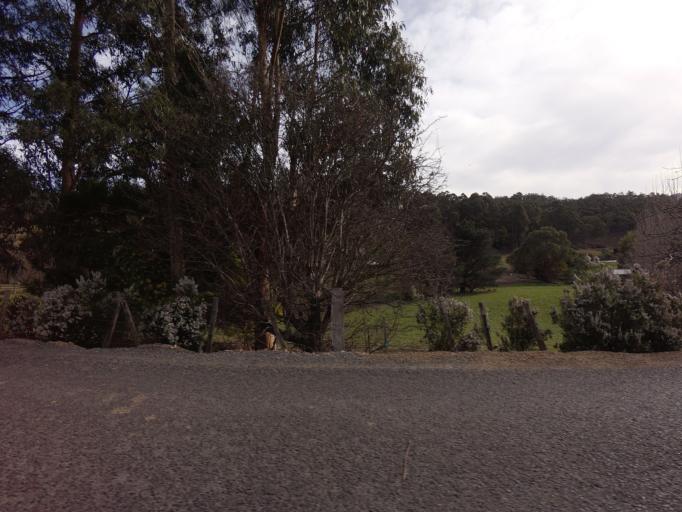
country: AU
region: Tasmania
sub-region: Kingborough
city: Margate
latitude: -42.9900
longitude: 147.1889
